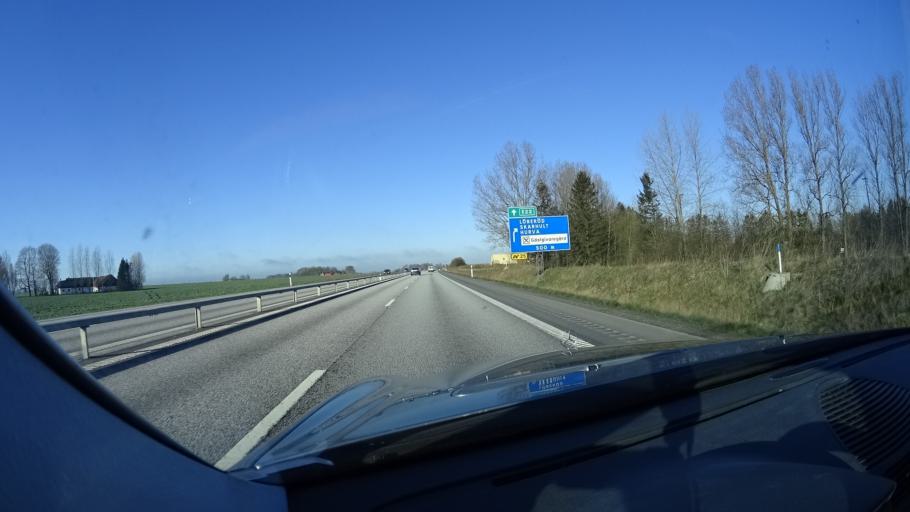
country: SE
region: Skane
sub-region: Hoors Kommun
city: Loberod
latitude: 55.7884
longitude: 13.4328
